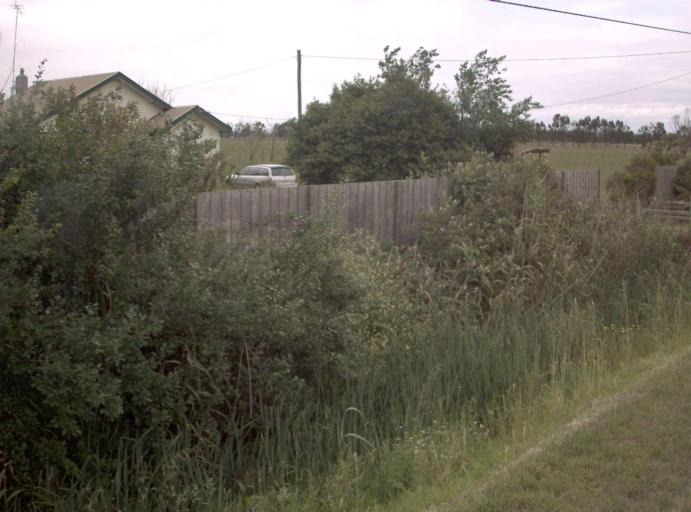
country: AU
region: Victoria
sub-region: Latrobe
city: Moe
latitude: -38.1985
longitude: 146.1512
